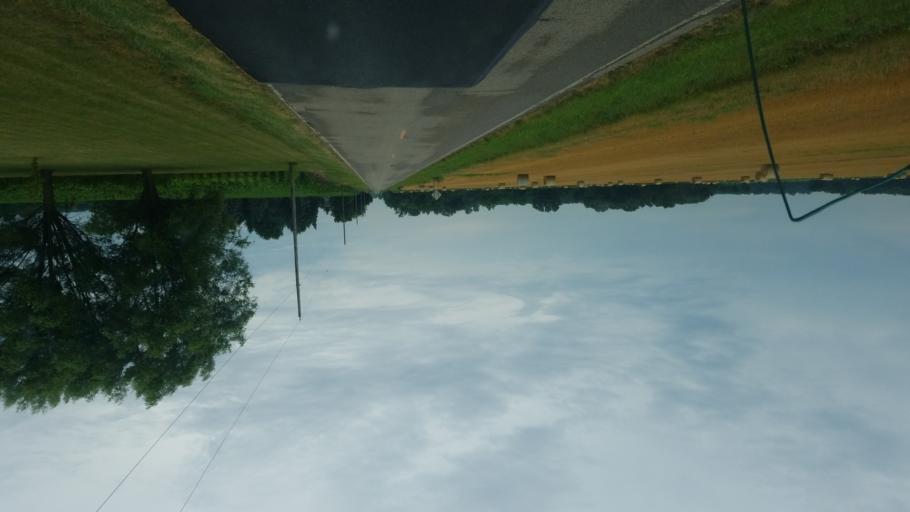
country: US
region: Ohio
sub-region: Defiance County
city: Hicksville
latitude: 41.2657
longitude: -84.6894
